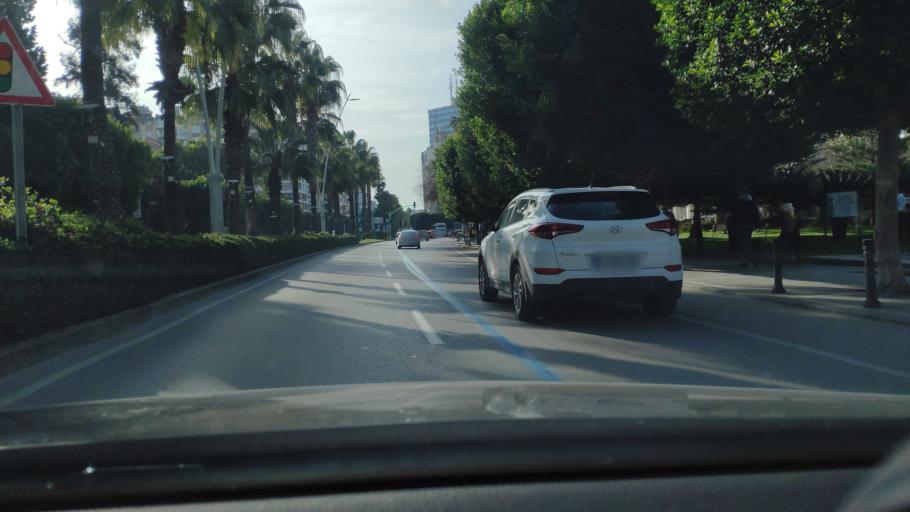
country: TR
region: Adana
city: Adana
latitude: 36.9976
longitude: 35.3244
